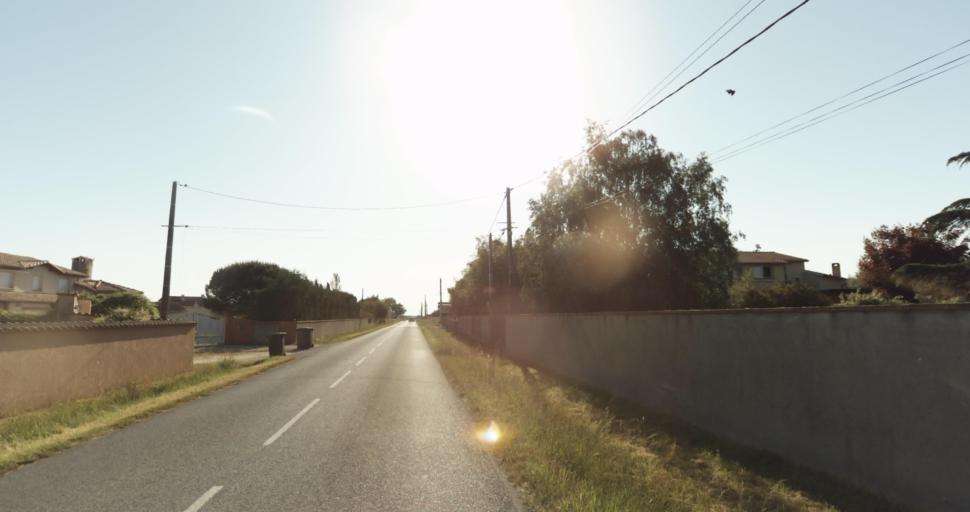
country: FR
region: Midi-Pyrenees
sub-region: Departement de la Haute-Garonne
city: Leguevin
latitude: 43.5754
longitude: 1.2335
